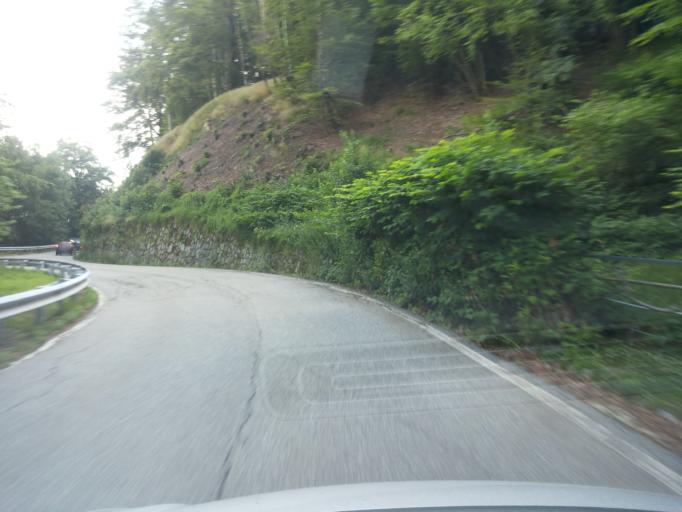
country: IT
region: Piedmont
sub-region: Provincia di Biella
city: Quittengo
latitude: 45.6624
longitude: 8.0217
